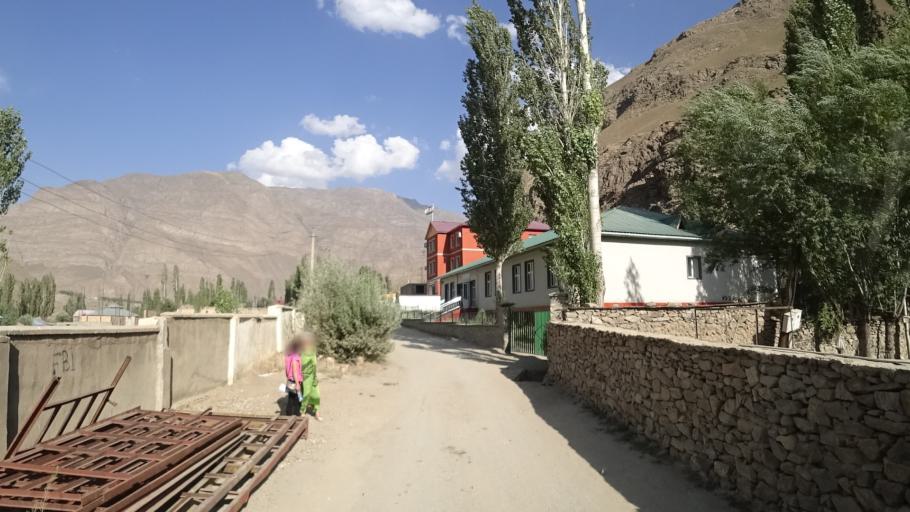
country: TJ
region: Gorno-Badakhshan
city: Khorugh
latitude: 37.4874
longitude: 71.5585
